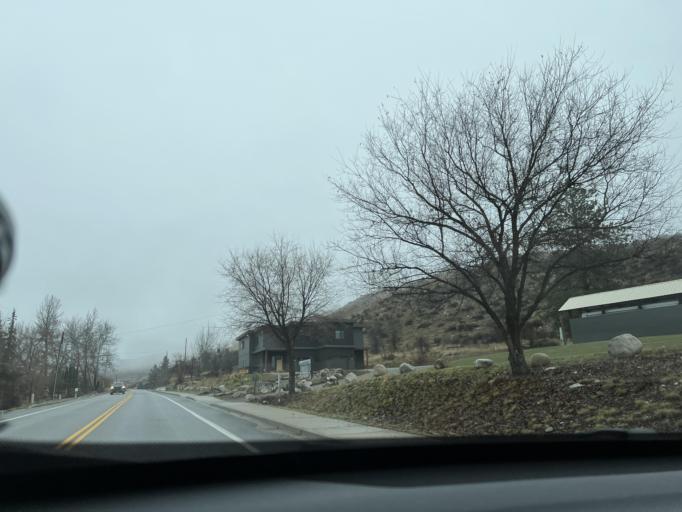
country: US
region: Washington
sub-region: Okanogan County
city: Brewster
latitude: 48.4807
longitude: -120.1796
